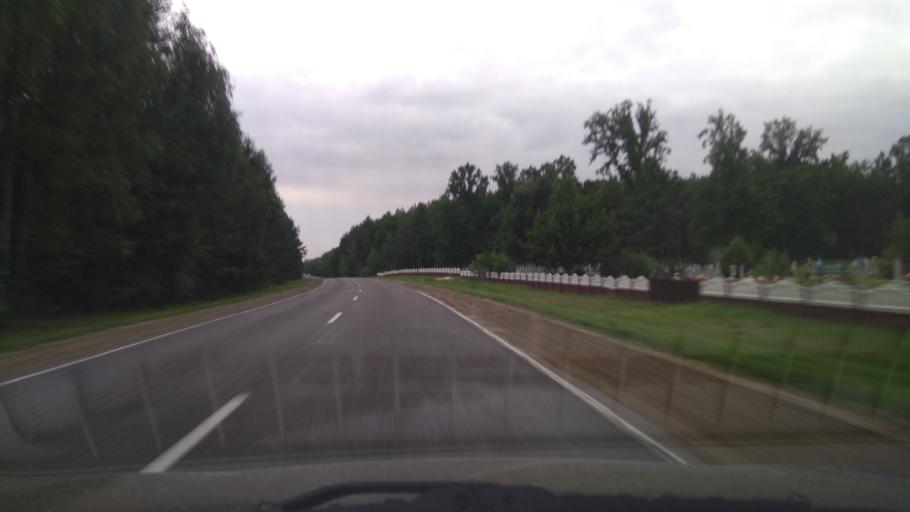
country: BY
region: Brest
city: Byaroza
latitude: 52.4047
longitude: 25.0004
